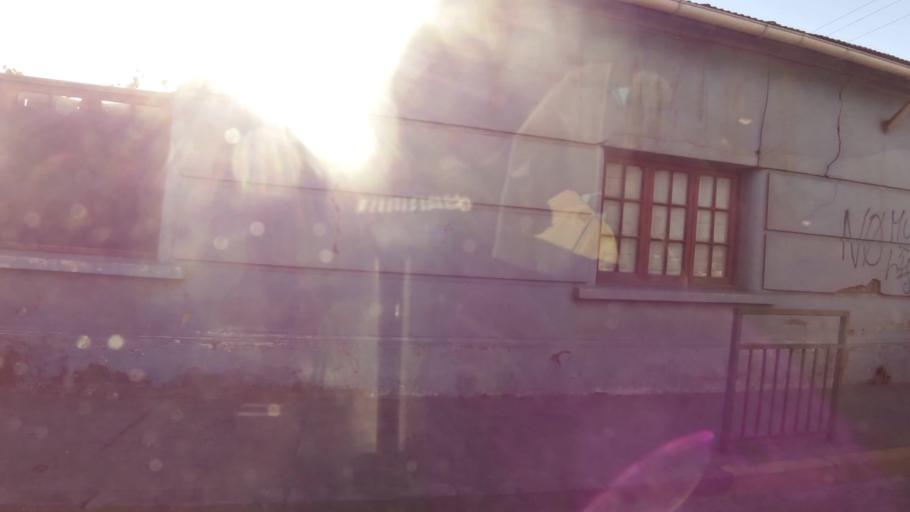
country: CL
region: O'Higgins
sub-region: Provincia de Colchagua
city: Chimbarongo
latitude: -34.5859
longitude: -70.9954
